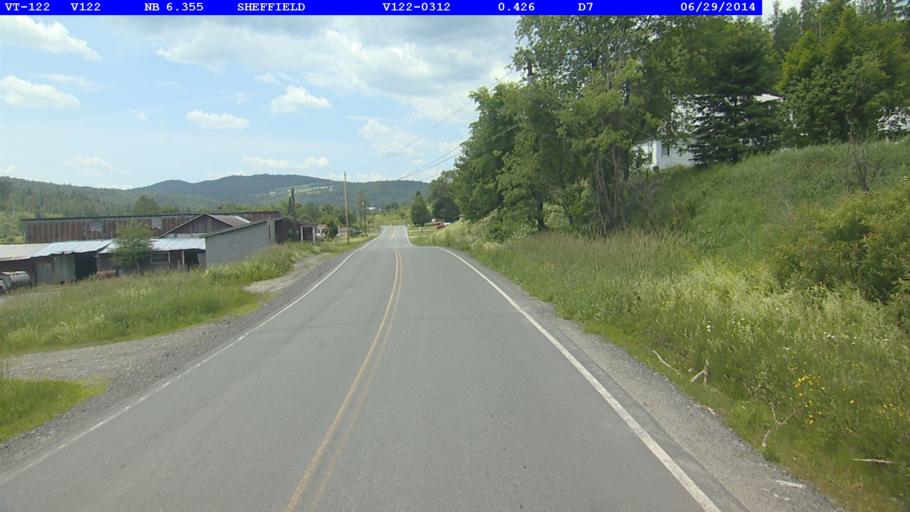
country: US
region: Vermont
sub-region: Caledonia County
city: Lyndonville
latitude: 44.5944
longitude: -72.0981
